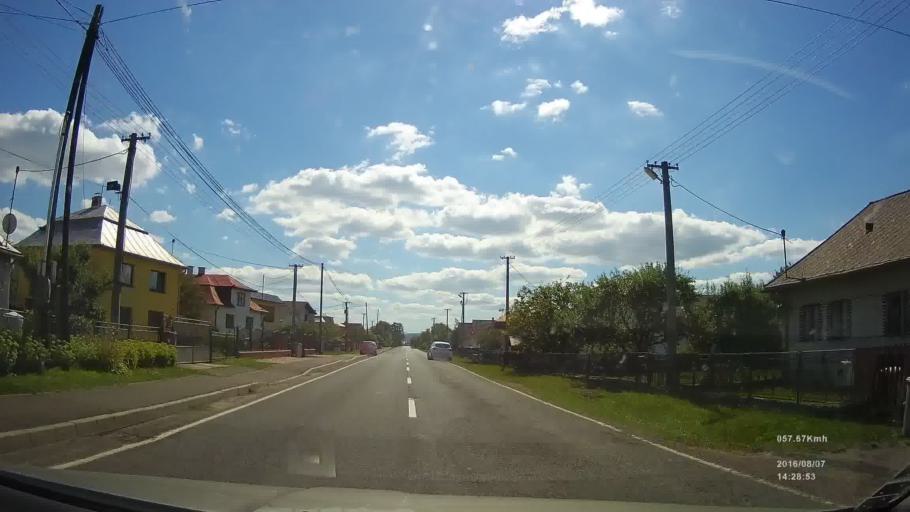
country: SK
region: Presovsky
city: Stropkov
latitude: 49.2461
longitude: 21.6823
